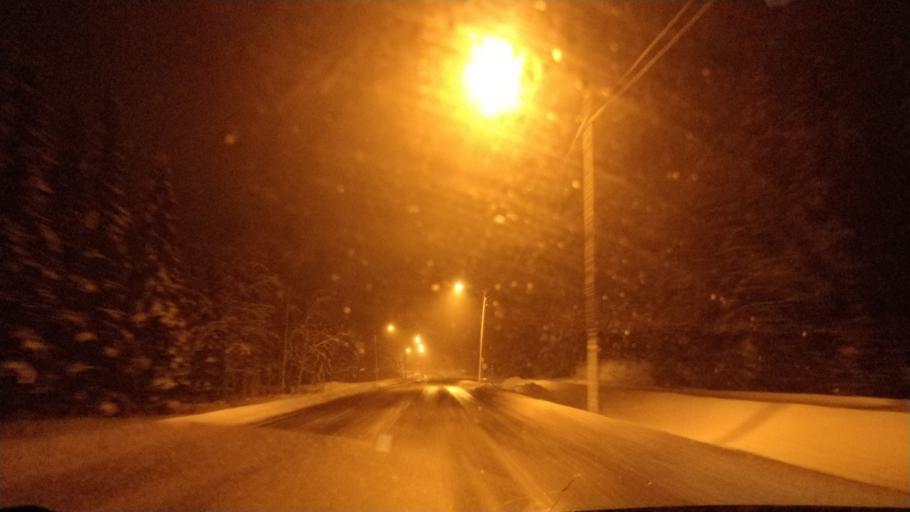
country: FI
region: Lapland
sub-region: Rovaniemi
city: Rovaniemi
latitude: 66.2776
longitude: 25.3327
